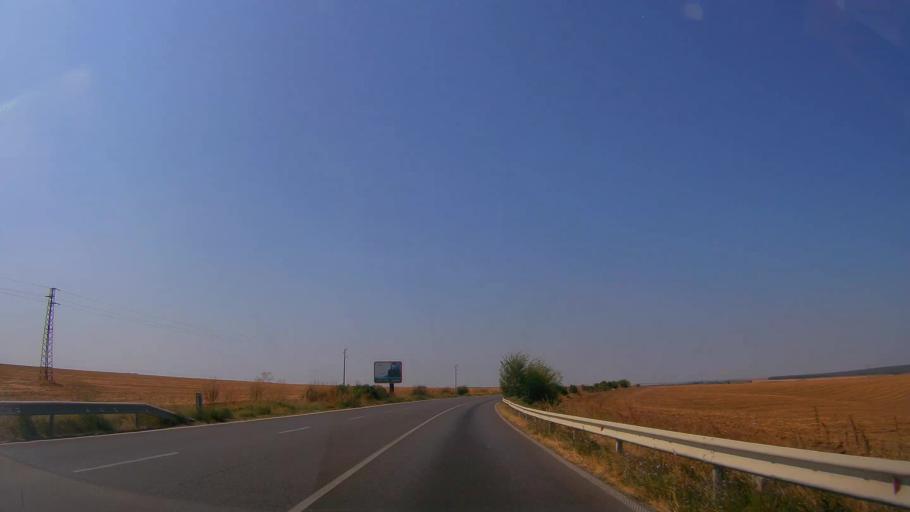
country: BG
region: Ruse
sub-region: Obshtina Vetovo
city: Senovo
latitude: 43.5623
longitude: 26.3452
